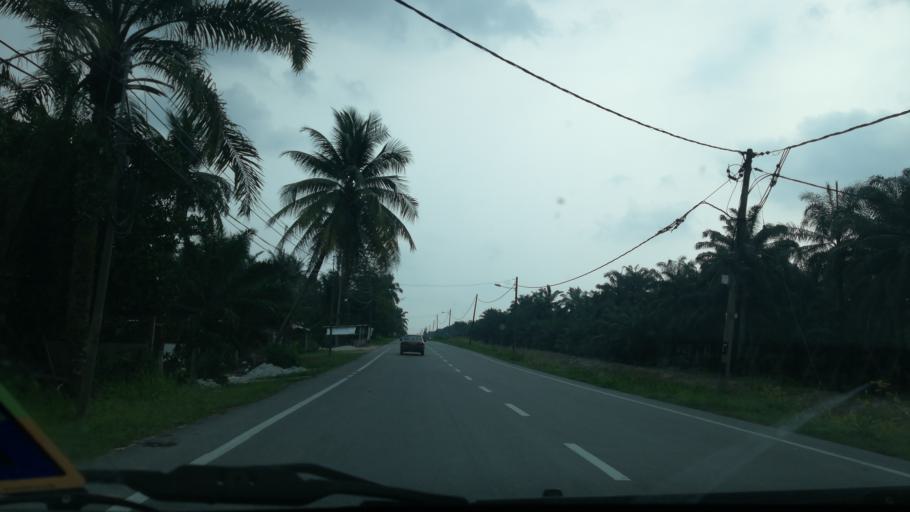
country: MY
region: Perak
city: Teluk Intan
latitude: 4.1152
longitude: 101.0718
